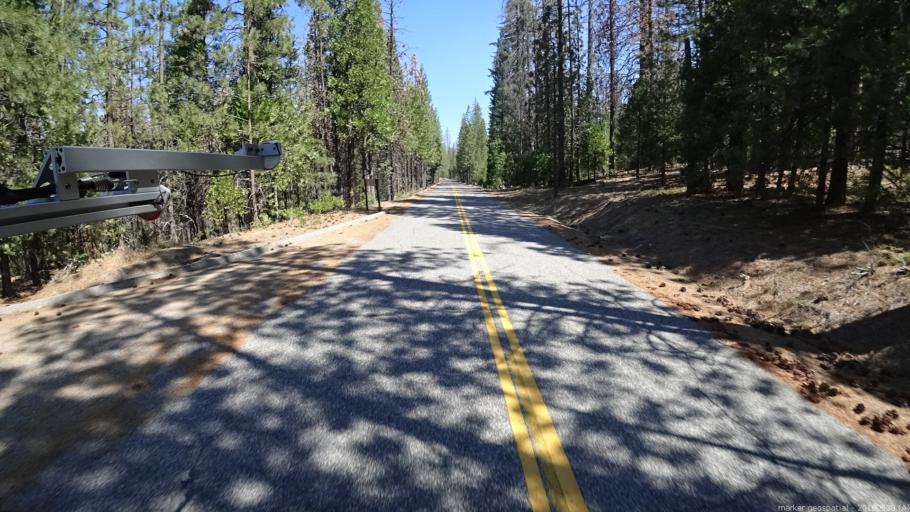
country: US
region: California
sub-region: Madera County
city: Oakhurst
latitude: 37.4045
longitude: -119.3476
